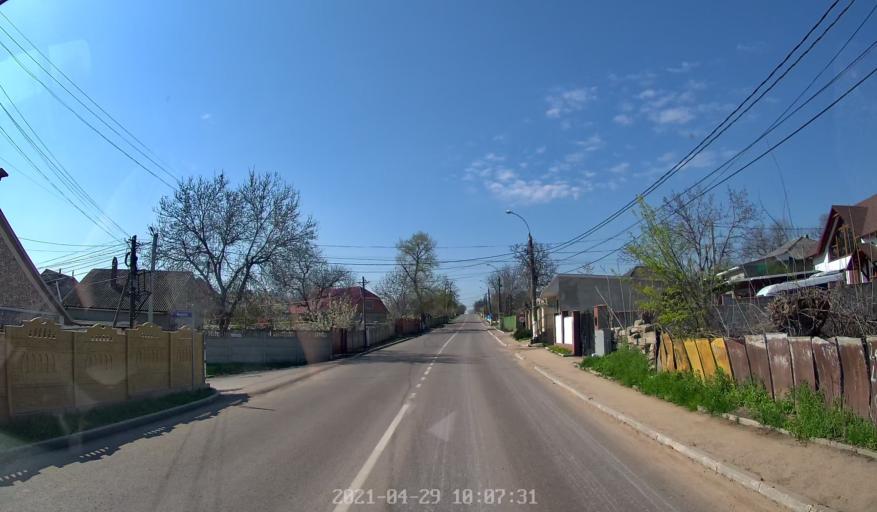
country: MD
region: Chisinau
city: Cricova
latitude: 47.1347
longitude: 28.8667
